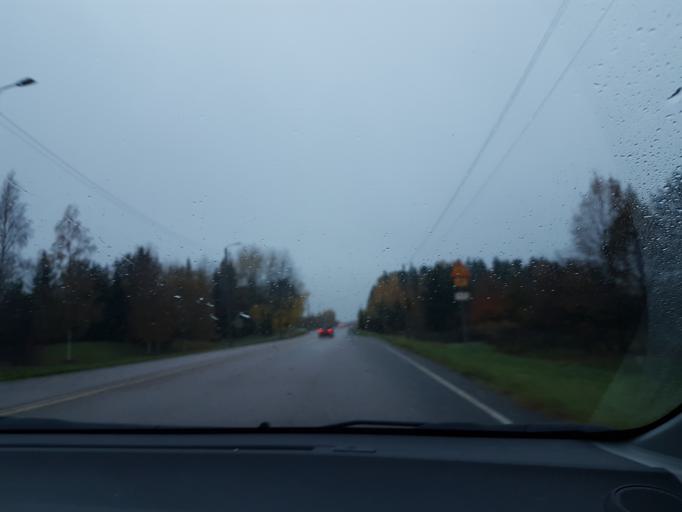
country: FI
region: Uusimaa
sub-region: Helsinki
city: Tuusula
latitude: 60.4186
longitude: 25.0530
